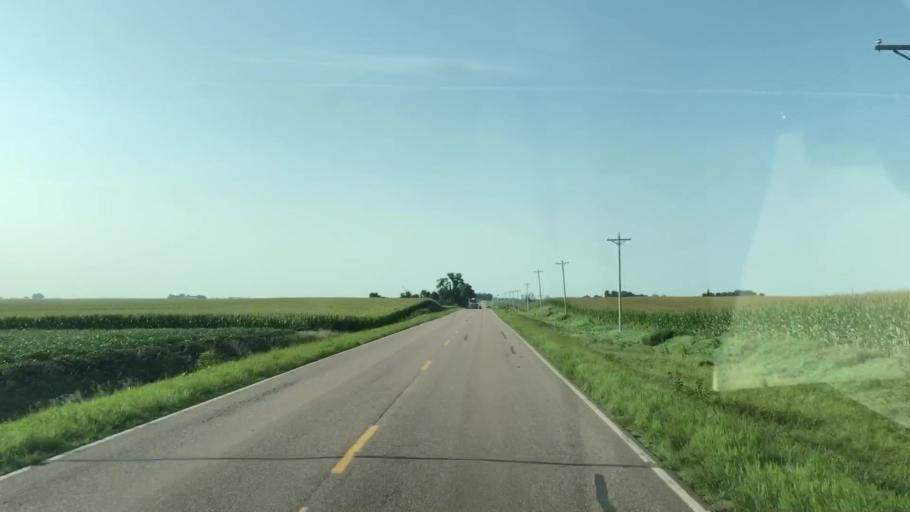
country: US
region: Iowa
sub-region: Lyon County
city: George
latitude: 43.2285
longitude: -96.0008
